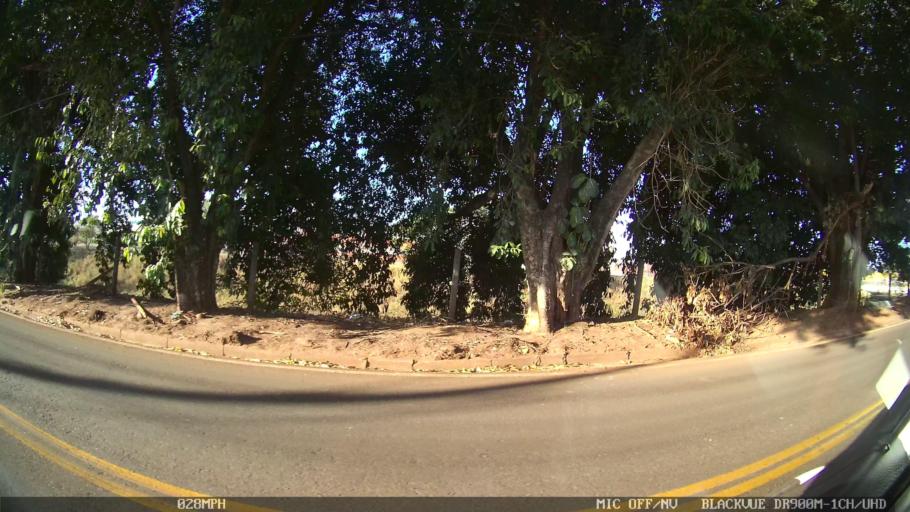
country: BR
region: Sao Paulo
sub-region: Sao Jose Do Rio Preto
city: Sao Jose do Rio Preto
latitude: -20.8504
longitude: -49.3445
